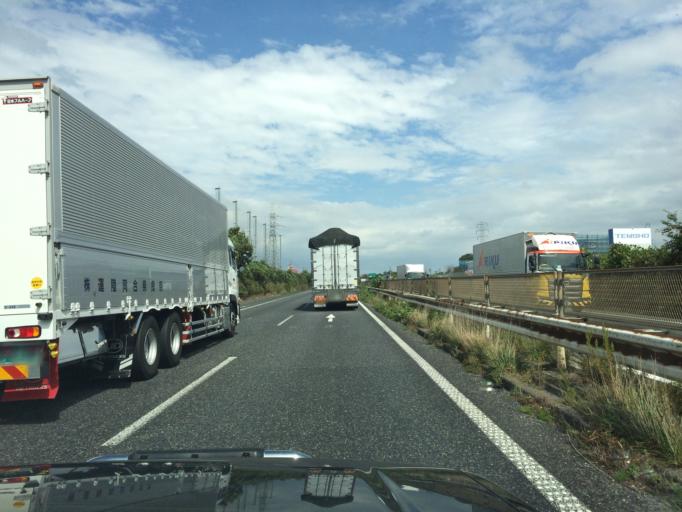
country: JP
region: Mie
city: Ueno-ebisumachi
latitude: 34.7177
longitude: 136.0813
